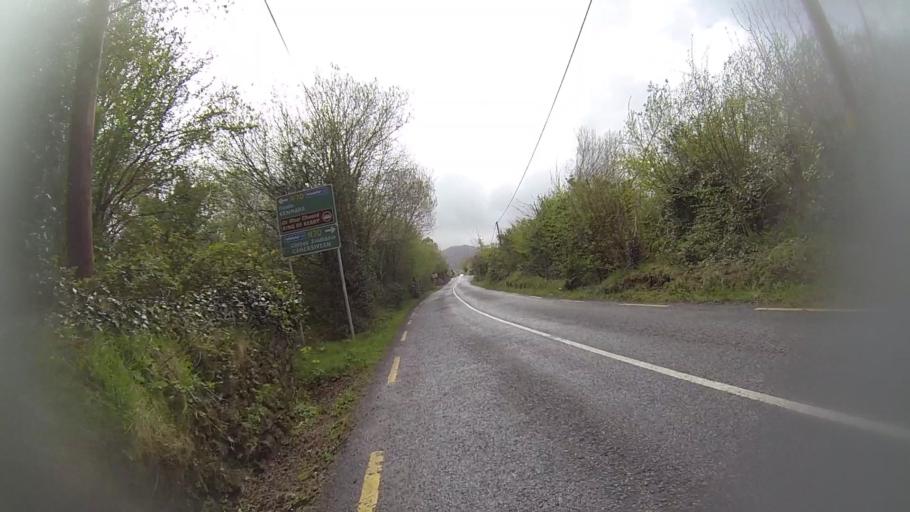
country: IE
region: Munster
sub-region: Ciarrai
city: Killorglin
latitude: 51.8400
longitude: -9.8945
